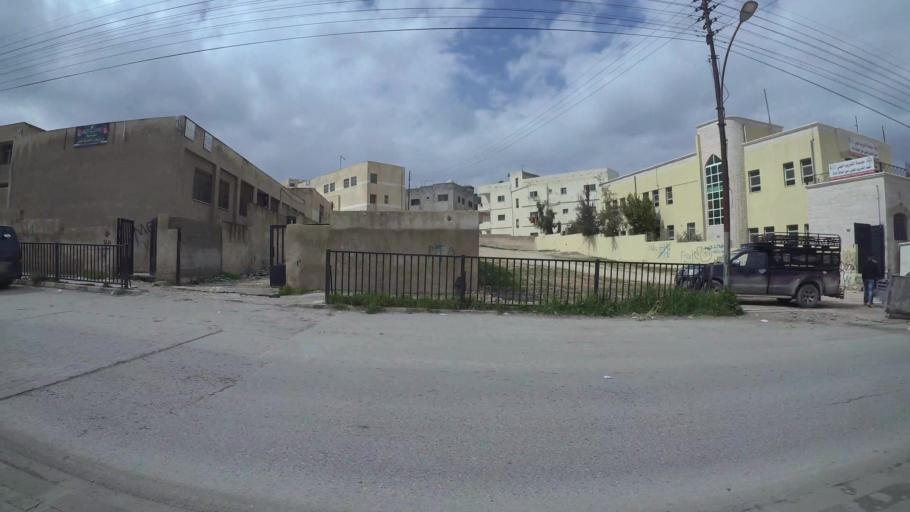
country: JO
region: Amman
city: Al Jubayhah
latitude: 32.0521
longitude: 35.8333
